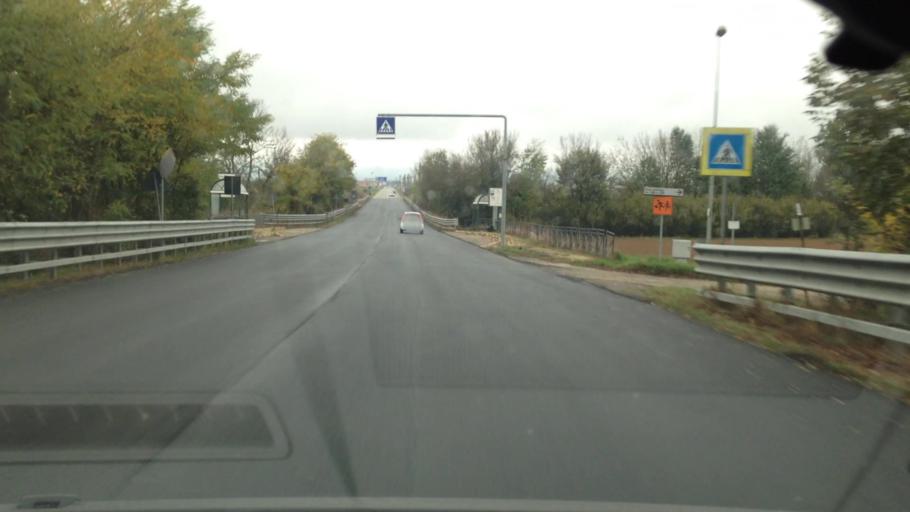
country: IT
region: Piedmont
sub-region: Provincia di Torino
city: Riva Presso Chieri
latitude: 44.9650
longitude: 7.9048
